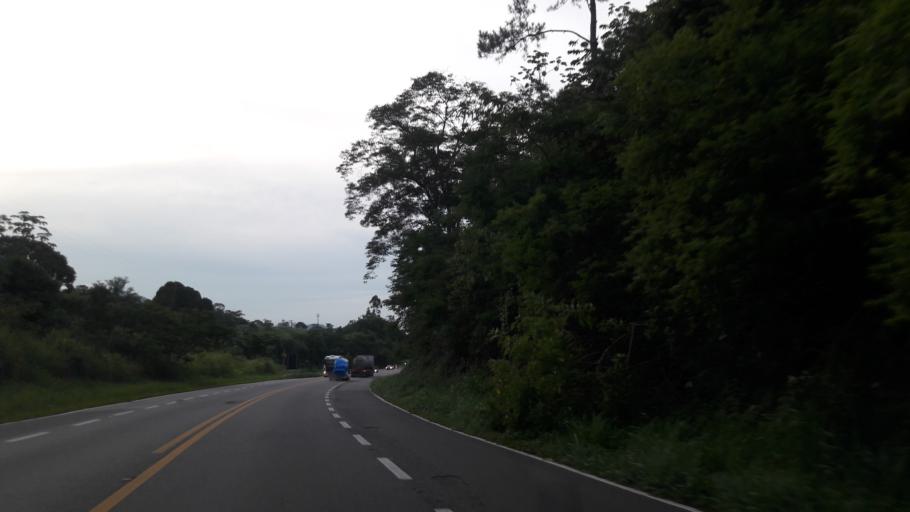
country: BR
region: Sao Paulo
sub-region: Miracatu
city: Miracatu
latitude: -24.2808
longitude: -47.2376
